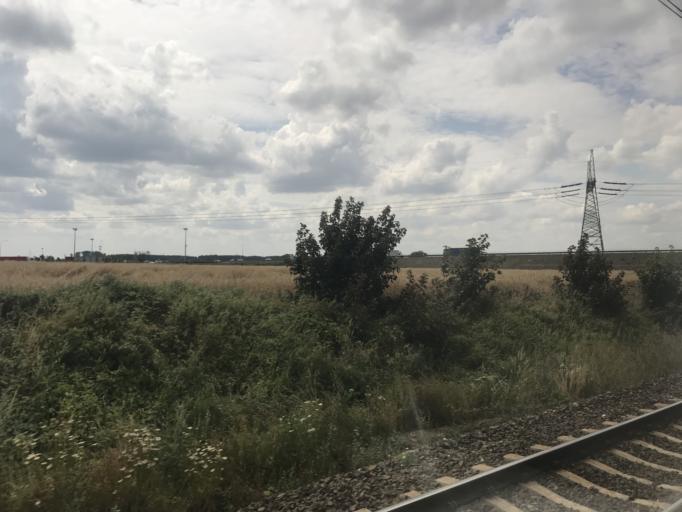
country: PL
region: Greater Poland Voivodeship
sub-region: Powiat poznanski
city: Plewiska
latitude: 52.3755
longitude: 16.7679
